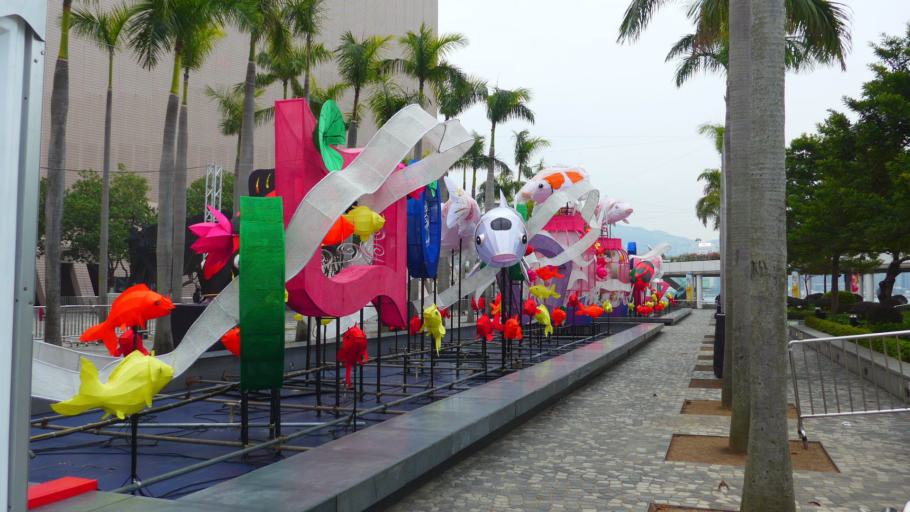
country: HK
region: Wanchai
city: Wan Chai
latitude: 22.2934
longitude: 114.1697
